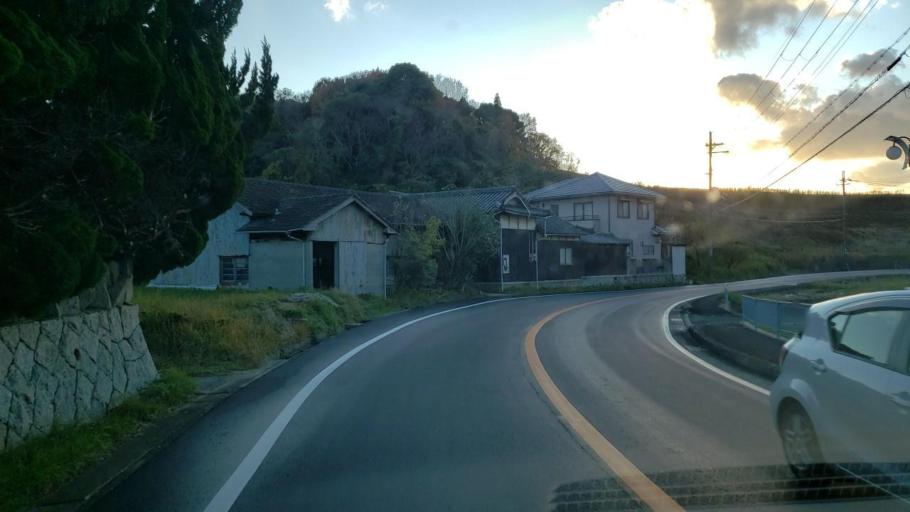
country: JP
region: Hyogo
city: Sumoto
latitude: 34.4009
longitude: 134.8293
